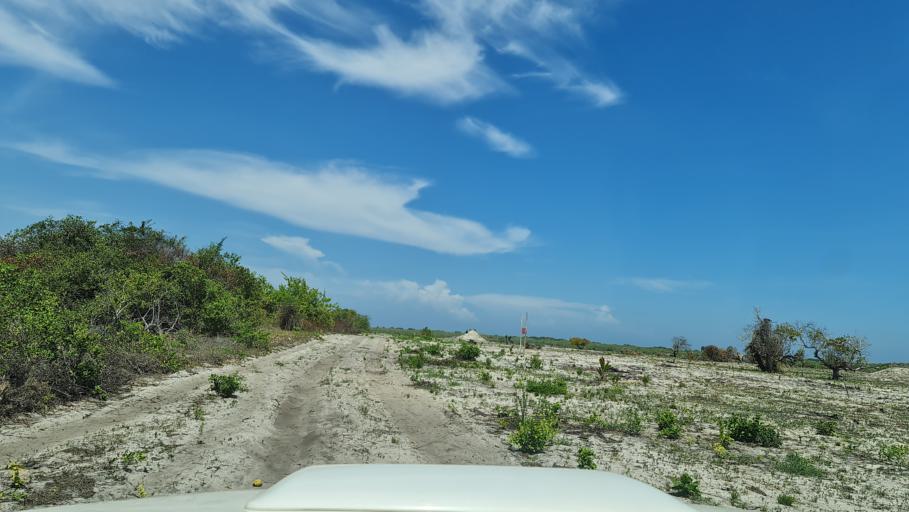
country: MZ
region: Nampula
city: Ilha de Mocambique
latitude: -15.1965
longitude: 40.6157
